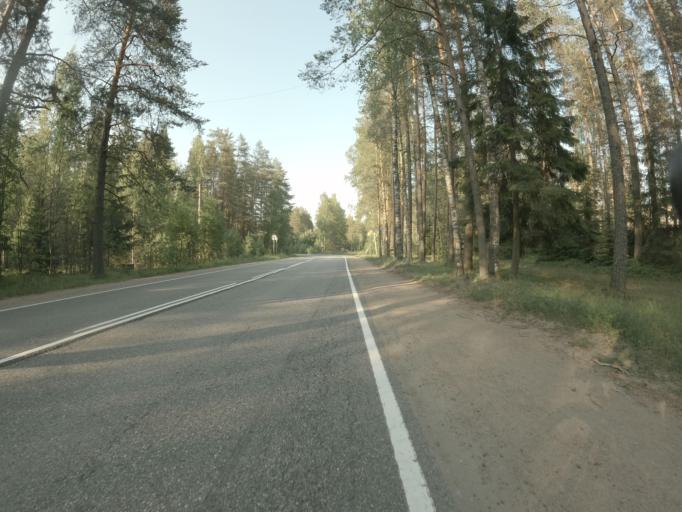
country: RU
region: Leningrad
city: Veshchevo
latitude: 60.4694
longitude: 29.2547
